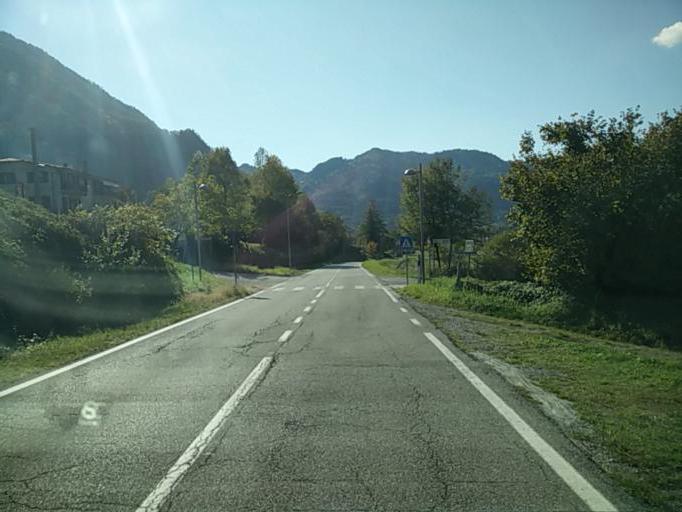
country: IT
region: Lombardy
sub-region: Provincia di Brescia
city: Crone
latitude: 45.7381
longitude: 10.4830
